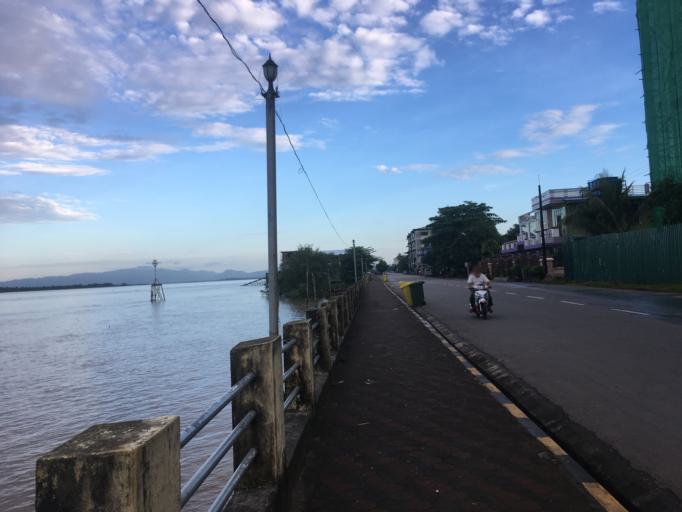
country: MM
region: Mon
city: Mawlamyine
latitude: 16.4704
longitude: 97.6211
